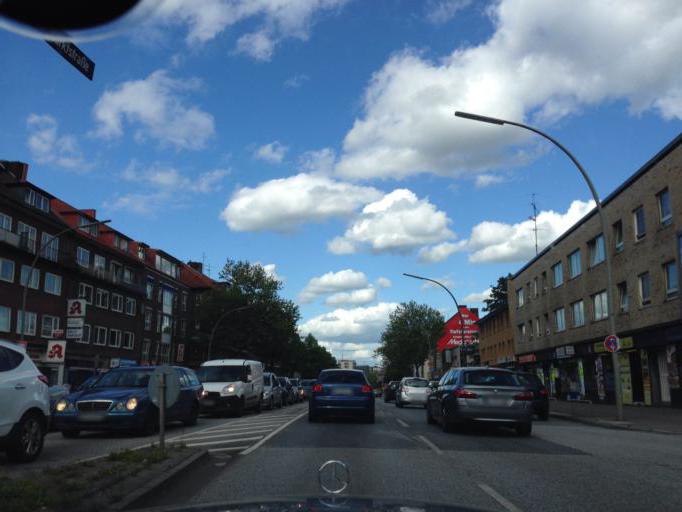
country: DE
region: Hamburg
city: Marienthal
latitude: 53.5732
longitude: 10.0706
